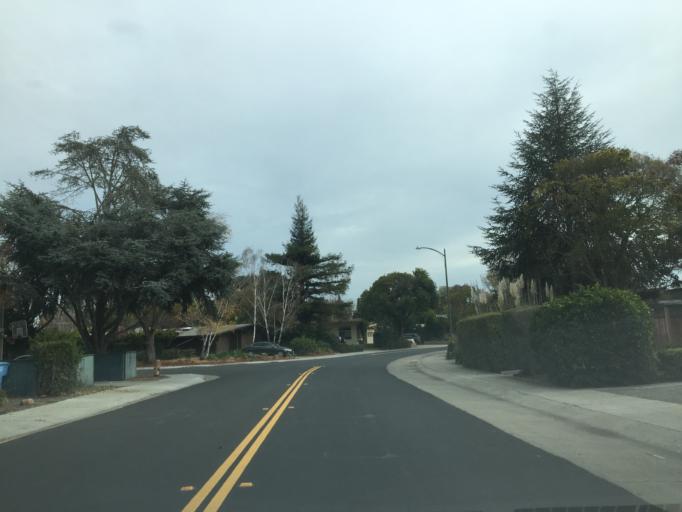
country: US
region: California
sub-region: Santa Clara County
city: Palo Alto
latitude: 37.4404
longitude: -122.1207
